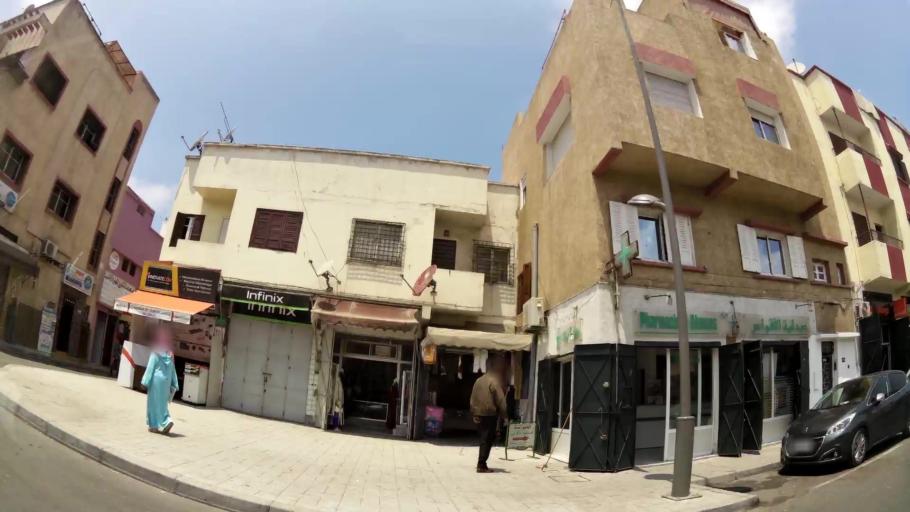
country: MA
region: Rabat-Sale-Zemmour-Zaer
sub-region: Skhirate-Temara
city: Temara
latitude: 33.9813
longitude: -6.8819
